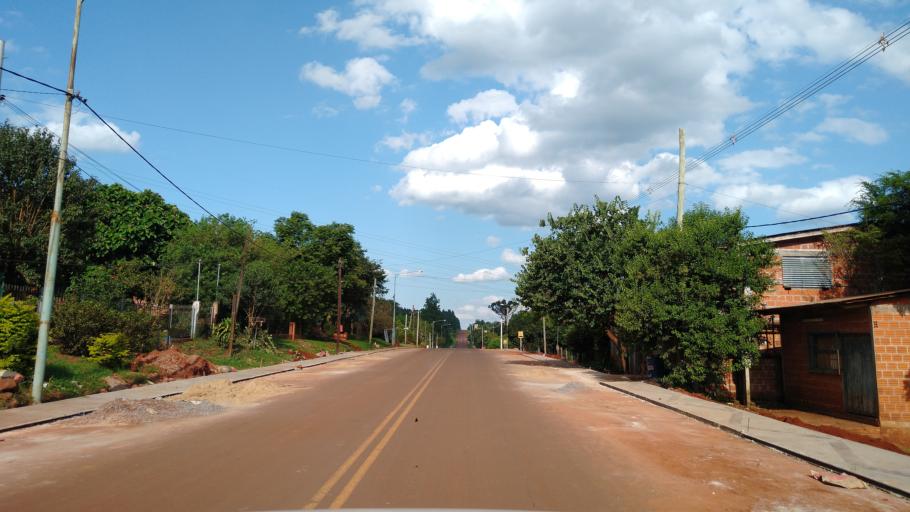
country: AR
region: Misiones
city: Puerto Piray
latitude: -26.4700
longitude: -54.6953
